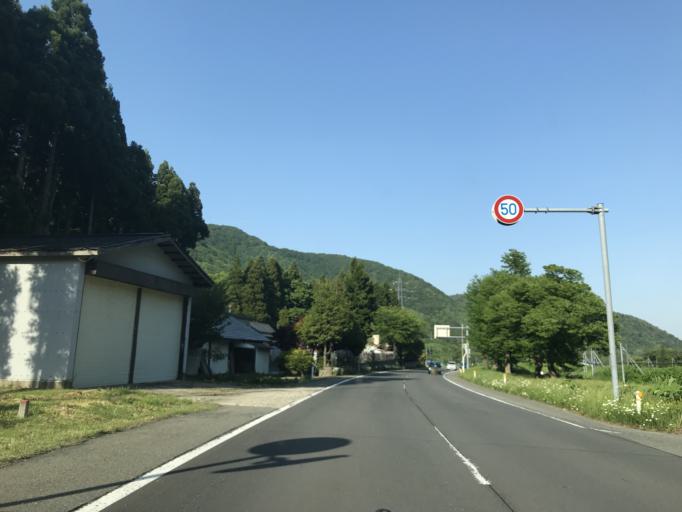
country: JP
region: Iwate
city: Kitakami
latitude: 39.3093
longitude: 140.9041
